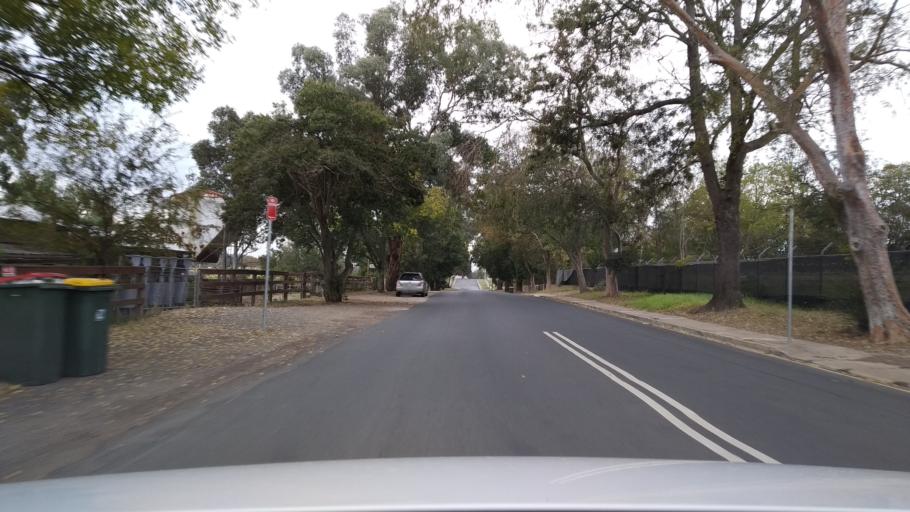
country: AU
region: New South Wales
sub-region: Camden
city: Elderslie
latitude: -34.0508
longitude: 150.6937
